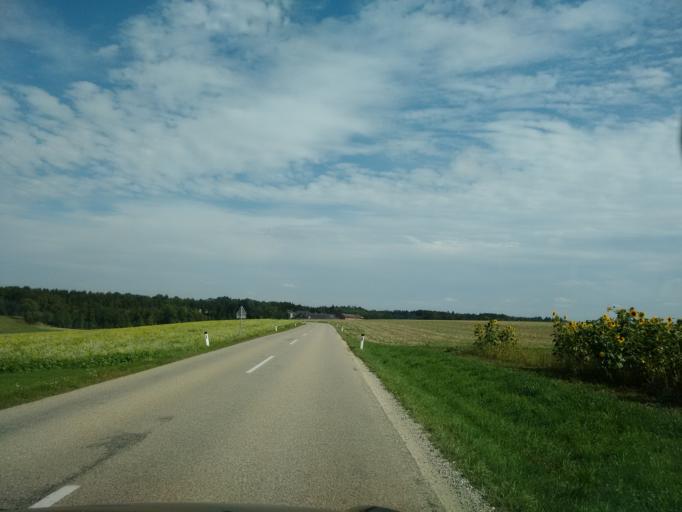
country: AT
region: Upper Austria
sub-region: Wels-Land
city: Thalheim bei Wels
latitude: 48.1318
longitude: 14.0651
